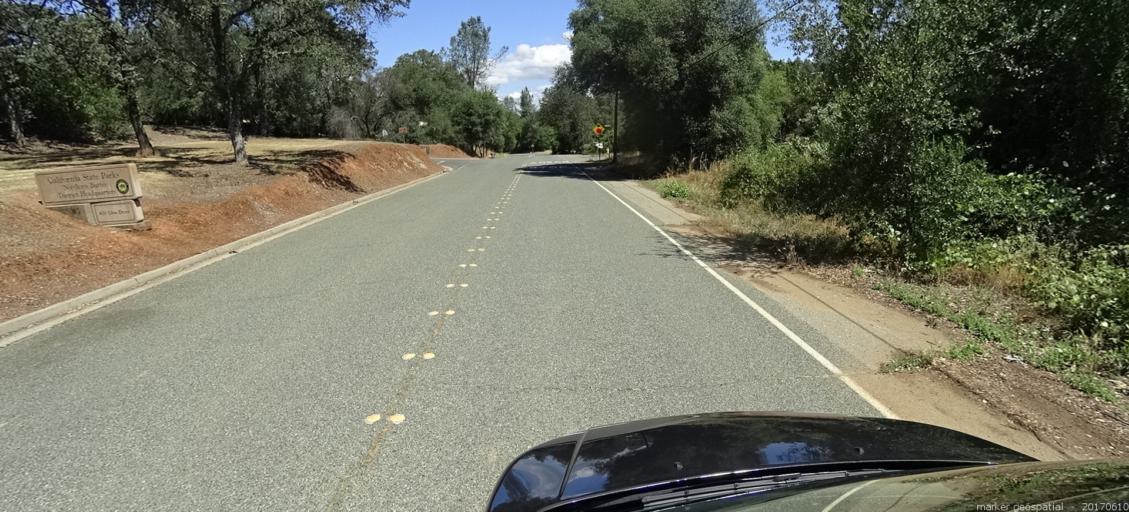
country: US
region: California
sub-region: Butte County
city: Oroville East
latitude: 39.5107
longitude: -121.5034
